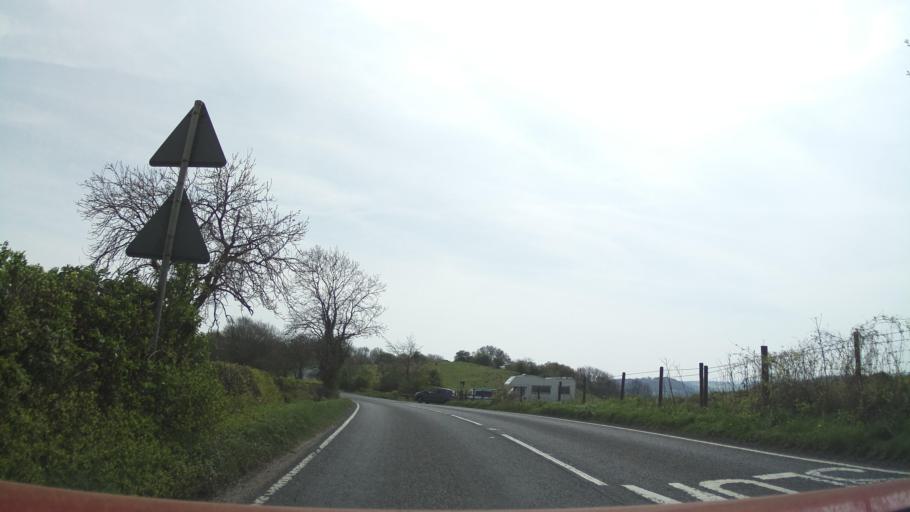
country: GB
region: England
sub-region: Somerset
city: Street
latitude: 51.1128
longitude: -2.7646
